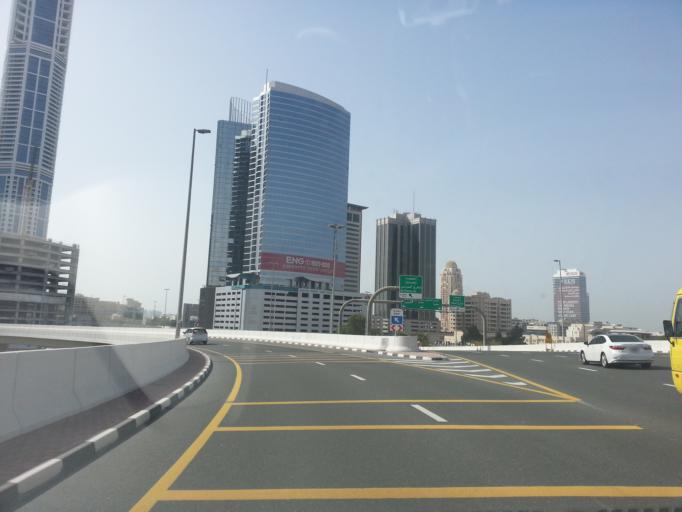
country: AE
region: Dubai
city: Dubai
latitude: 25.0865
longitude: 55.1540
